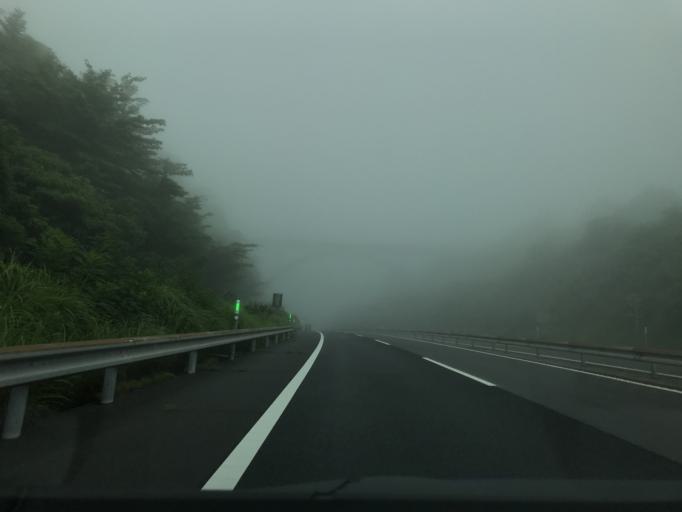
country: JP
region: Oita
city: Hiji
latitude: 33.3635
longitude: 131.4519
